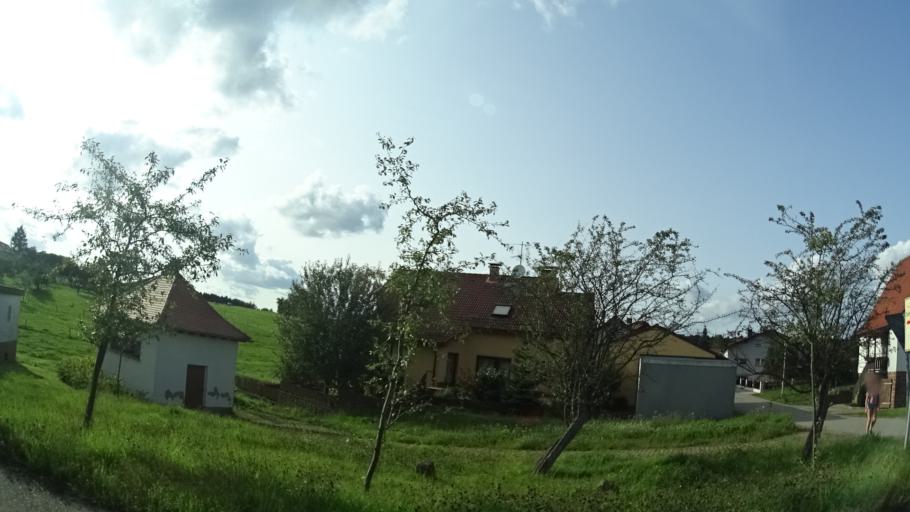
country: DE
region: Hesse
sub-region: Regierungsbezirk Darmstadt
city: Hesseneck
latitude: 49.5750
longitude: 9.0876
